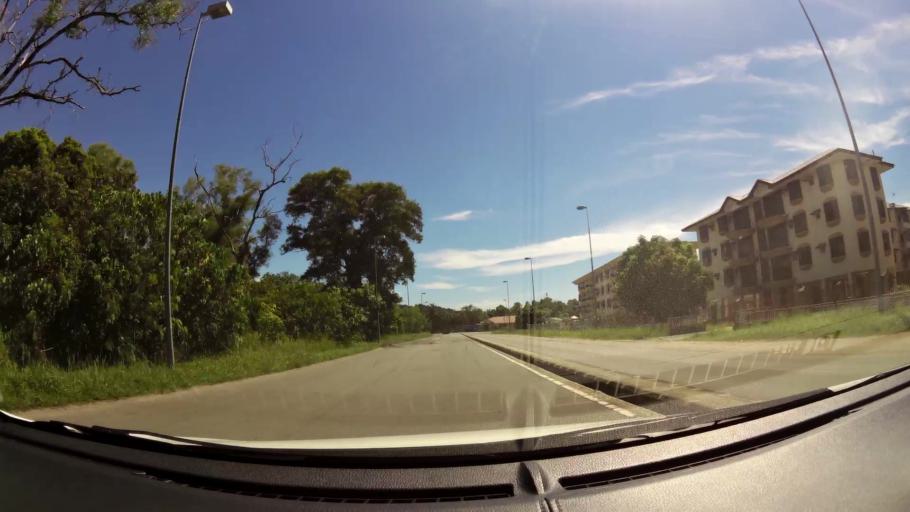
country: BN
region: Brunei and Muara
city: Bandar Seri Begawan
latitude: 5.0237
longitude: 115.0639
